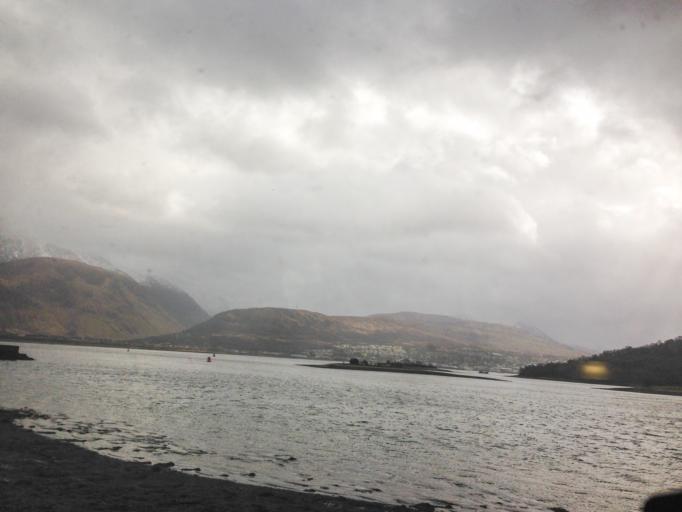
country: GB
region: Scotland
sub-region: Highland
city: Fort William
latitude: 56.8430
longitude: -5.1277
